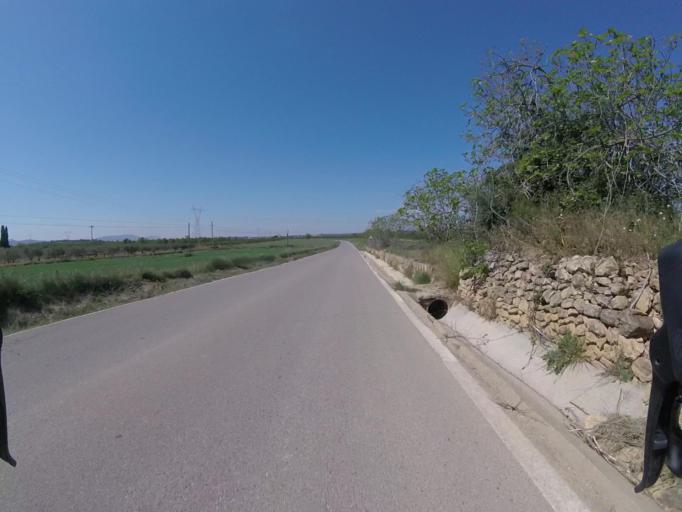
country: ES
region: Valencia
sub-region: Provincia de Castello
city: Benlloch
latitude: 40.2194
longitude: 0.0424
